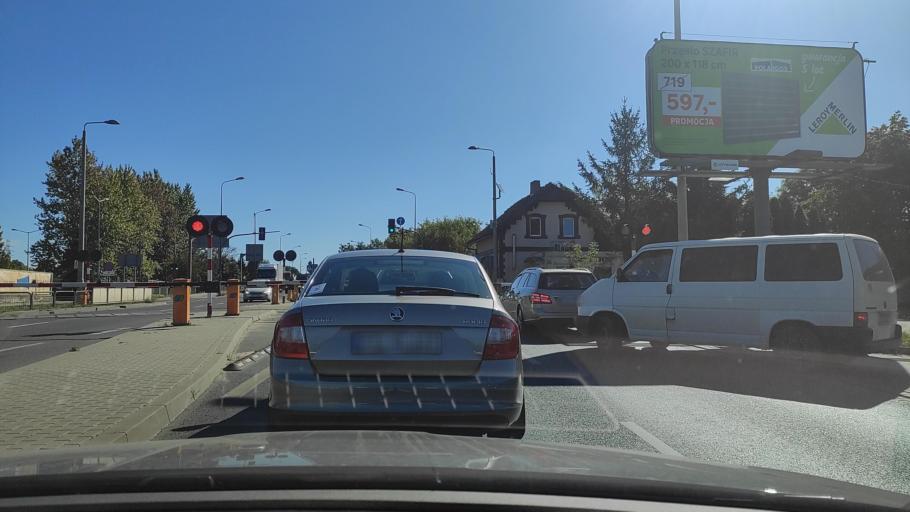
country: PL
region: Greater Poland Voivodeship
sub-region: Powiat poznanski
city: Czerwonak
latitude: 52.4263
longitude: 16.9788
